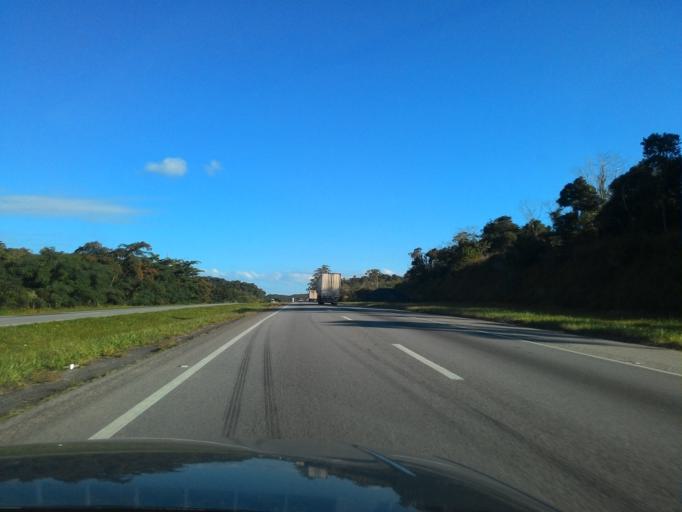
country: BR
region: Sao Paulo
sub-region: Registro
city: Registro
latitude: -24.5503
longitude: -47.8637
